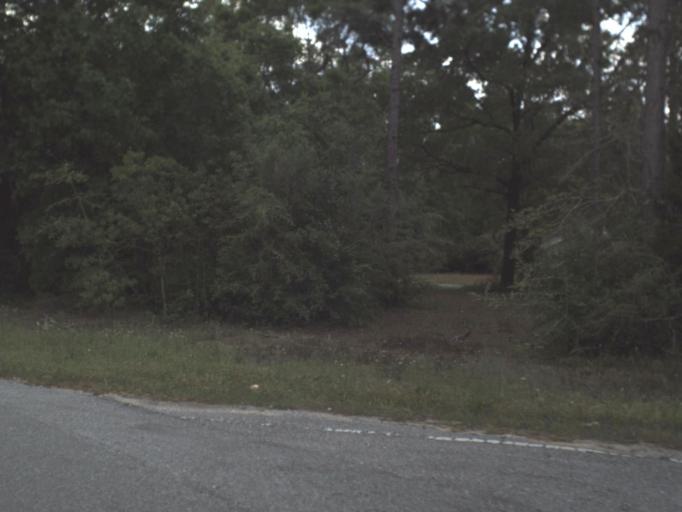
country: US
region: Florida
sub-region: Escambia County
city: Molino
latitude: 30.7911
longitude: -87.4147
